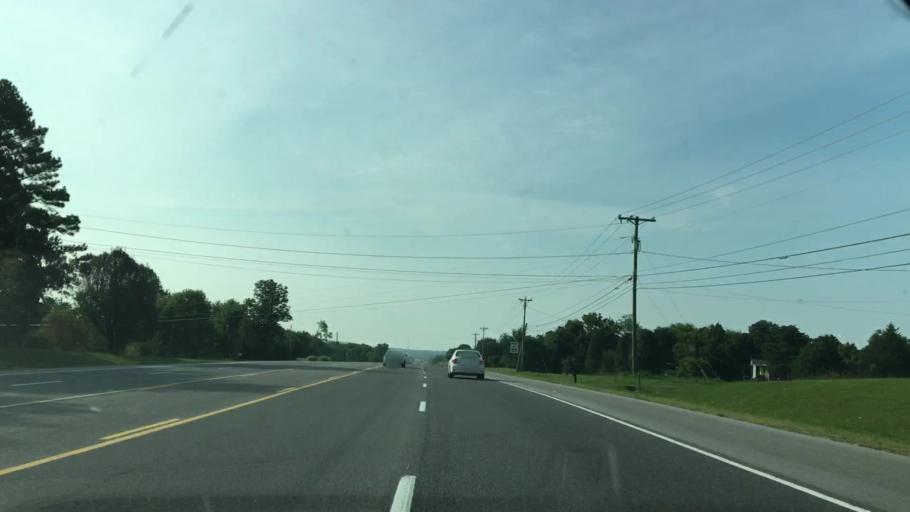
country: US
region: Tennessee
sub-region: Wilson County
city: Mount Juliet
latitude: 36.2072
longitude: -86.4192
